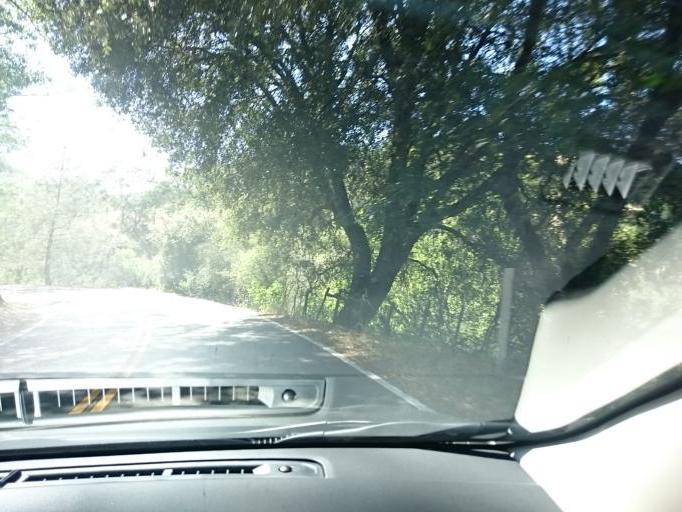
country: US
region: California
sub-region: Santa Clara County
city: East Foothills
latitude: 37.3276
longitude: -121.6705
